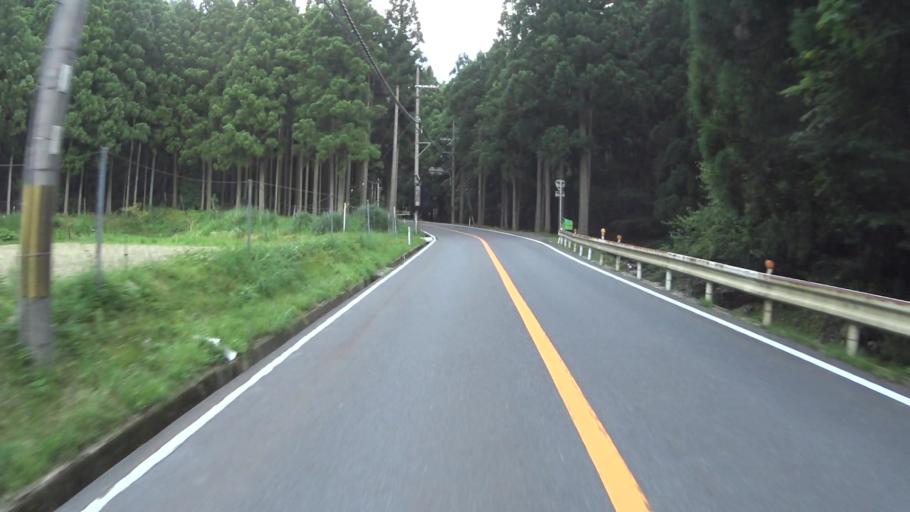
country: JP
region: Kyoto
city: Kameoka
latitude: 35.2602
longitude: 135.6106
